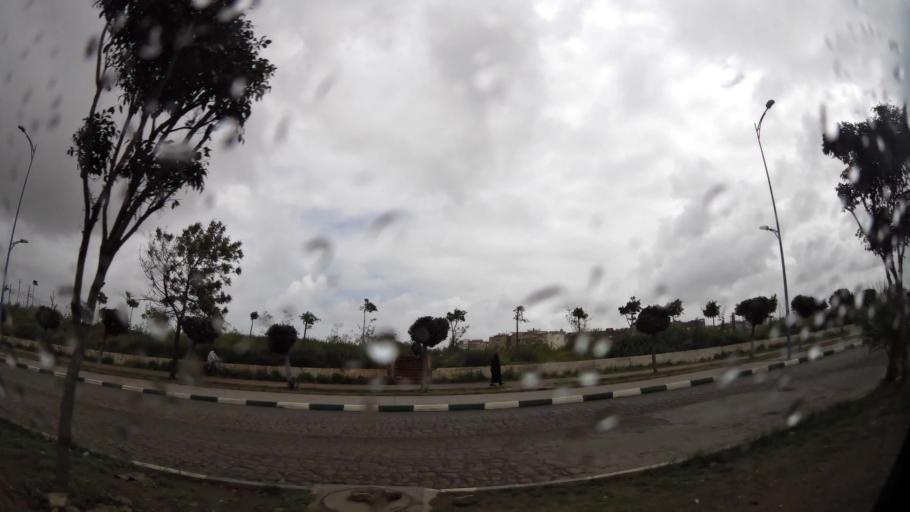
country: MA
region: Grand Casablanca
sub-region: Mediouna
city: Tit Mellil
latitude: 33.6178
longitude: -7.5004
